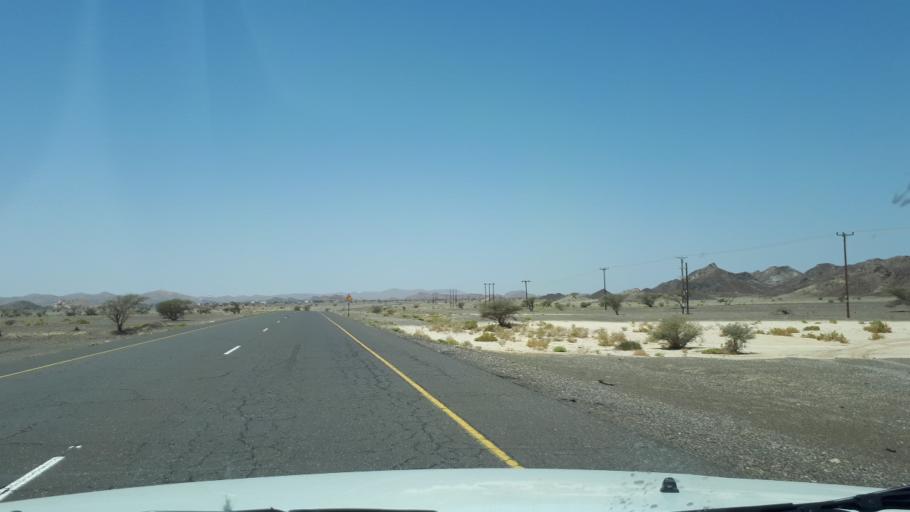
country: OM
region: Ash Sharqiyah
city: Ibra'
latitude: 22.6212
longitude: 58.4459
